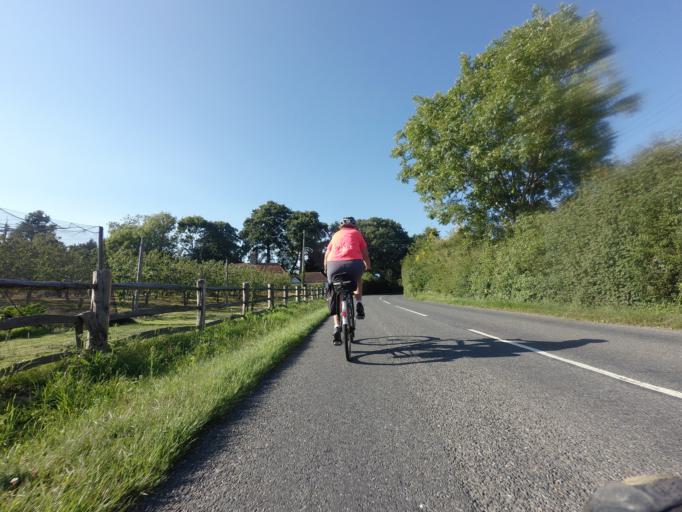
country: GB
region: England
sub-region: Kent
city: Tenterden
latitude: 51.0556
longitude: 0.6917
